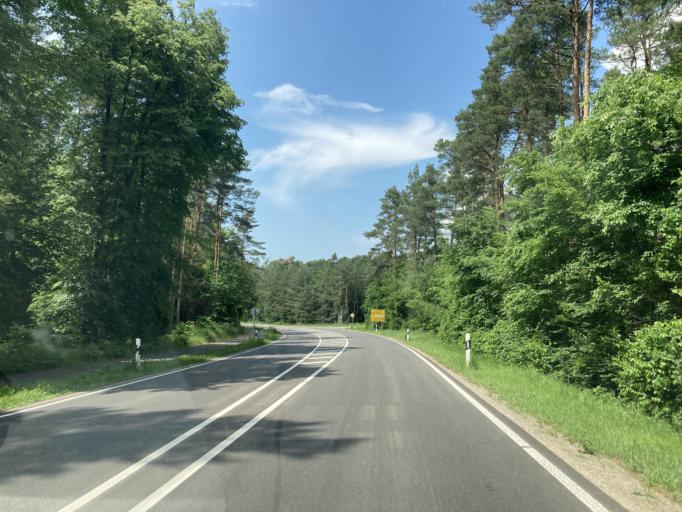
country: DE
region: Baden-Wuerttemberg
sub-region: Karlsruhe Region
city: Eggenstein-Leopoldshafen
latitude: 49.0900
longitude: 8.4482
